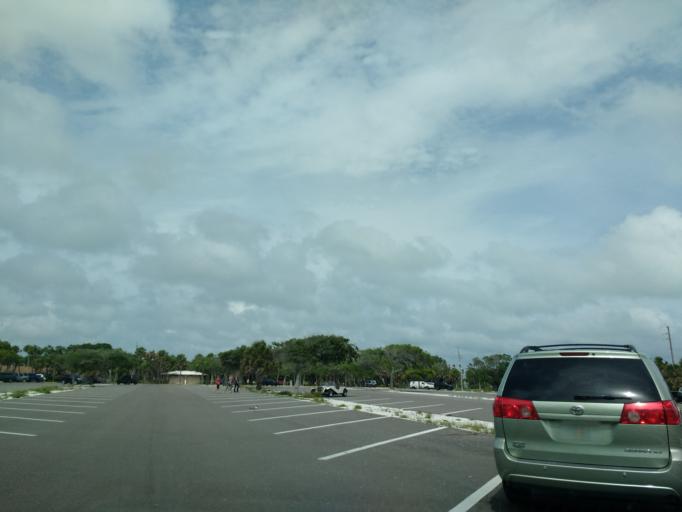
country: US
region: Florida
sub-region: Pinellas County
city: Tierra Verde
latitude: 27.6140
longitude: -82.7366
